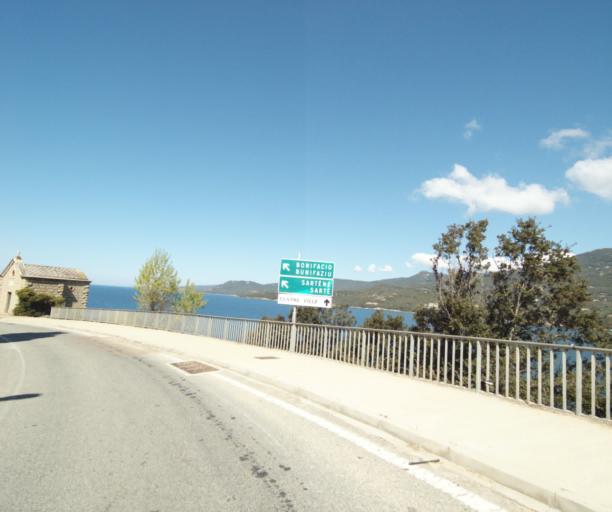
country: FR
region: Corsica
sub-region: Departement de la Corse-du-Sud
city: Propriano
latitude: 41.6797
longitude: 8.9127
